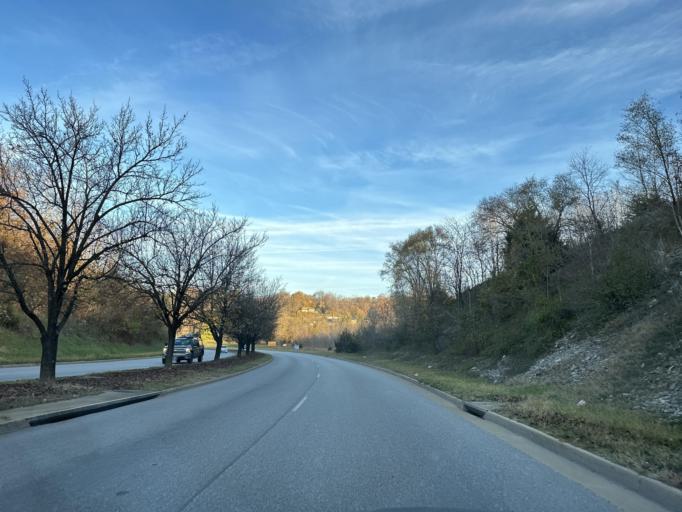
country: US
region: Virginia
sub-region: City of Staunton
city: Staunton
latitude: 38.1513
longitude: -79.0524
